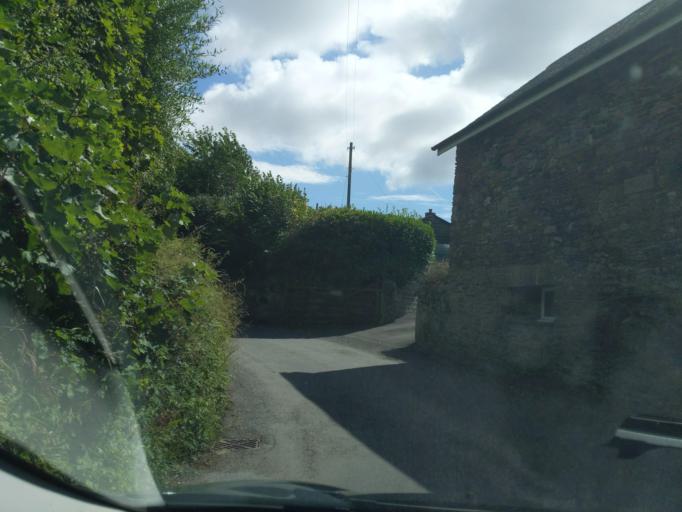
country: GB
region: England
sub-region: Devon
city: Ivybridge
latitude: 50.3729
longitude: -3.9048
